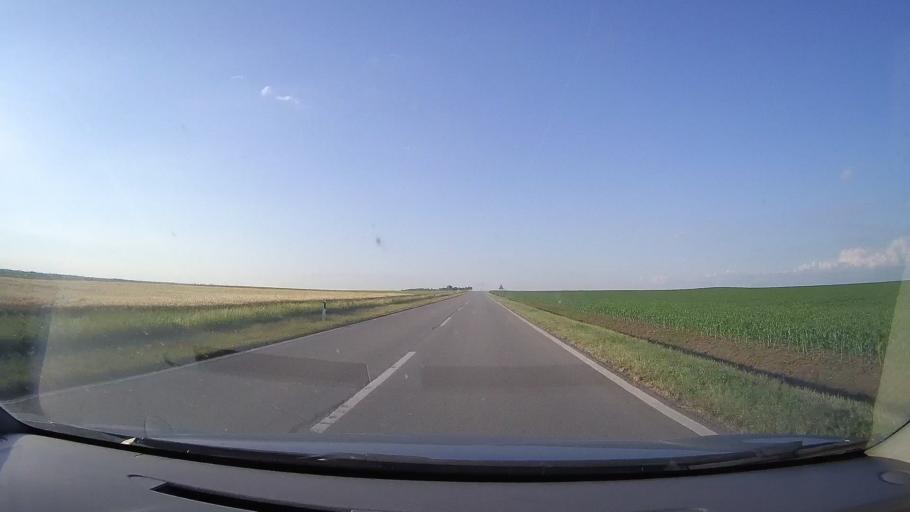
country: RO
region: Timis
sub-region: Comuna Moravita
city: Moravita
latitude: 45.1909
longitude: 21.2986
